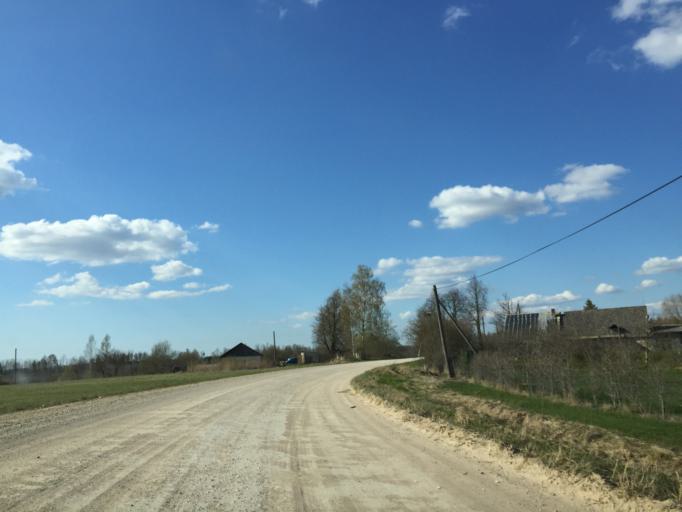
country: LV
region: Saulkrastu
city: Saulkrasti
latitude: 57.3468
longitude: 24.5791
